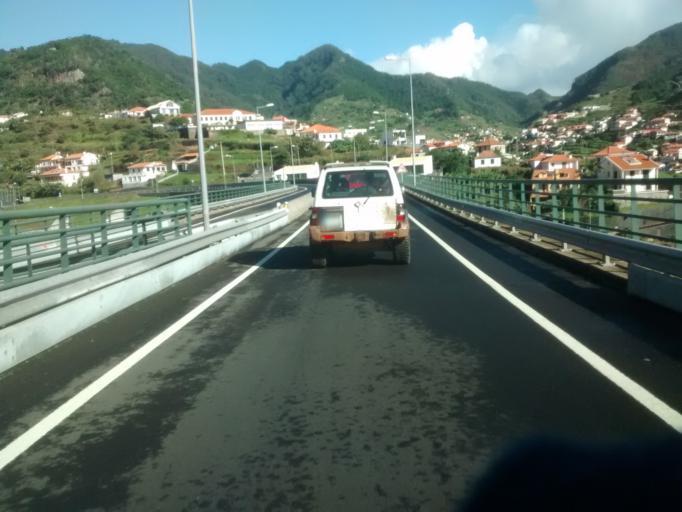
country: PT
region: Madeira
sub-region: Machico
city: Machico
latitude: 32.7277
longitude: -16.7790
